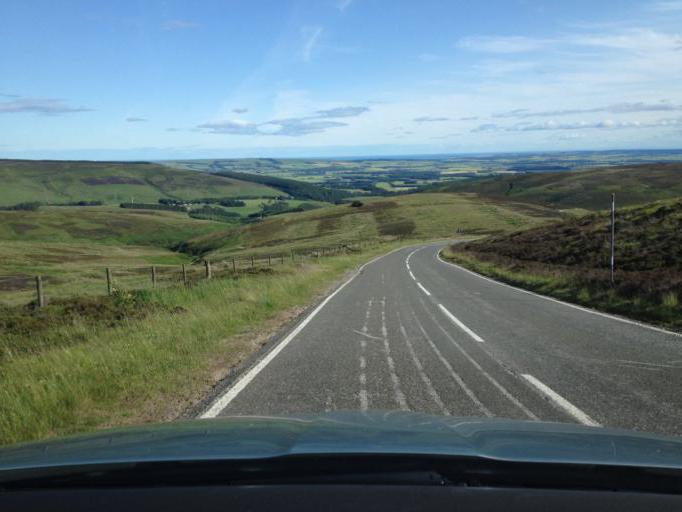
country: GB
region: Scotland
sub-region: Aberdeenshire
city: Laurencekirk
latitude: 56.9147
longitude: -2.5729
